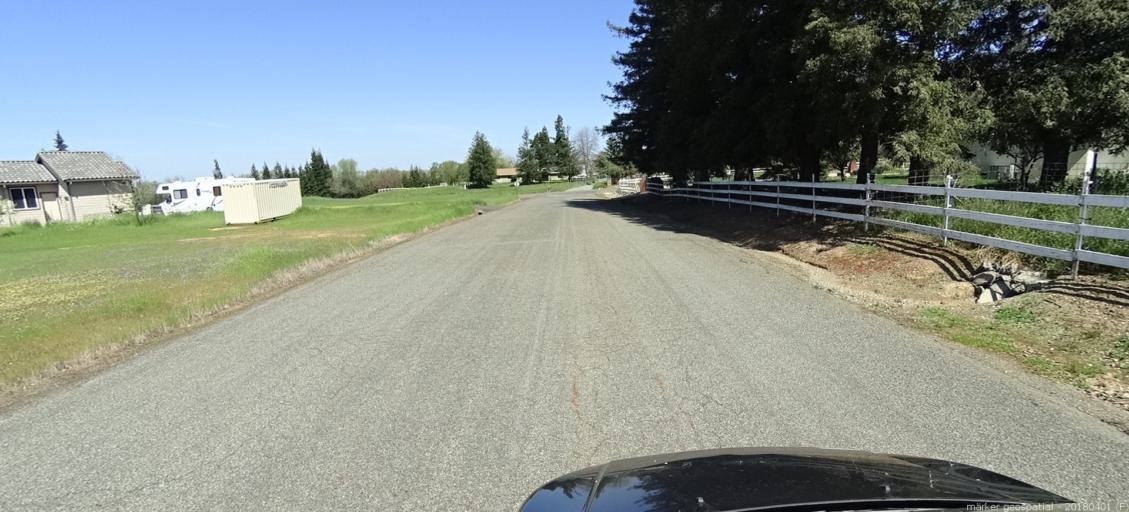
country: US
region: California
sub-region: Sacramento County
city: Wilton
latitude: 38.4164
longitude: -121.2216
